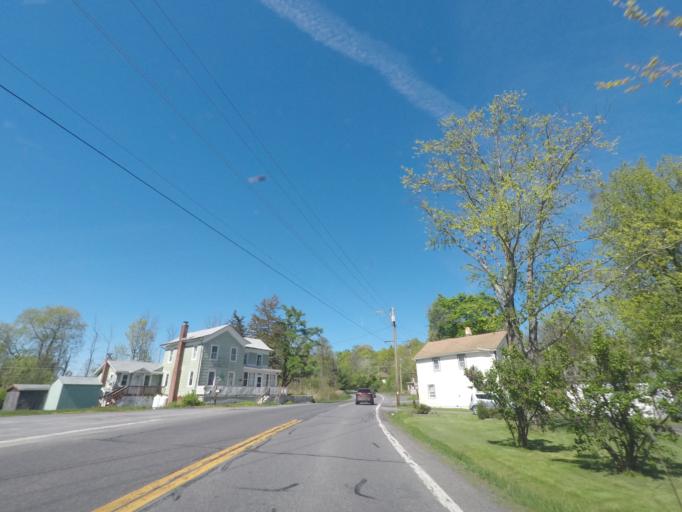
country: US
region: New York
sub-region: Ulster County
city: Saugerties
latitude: 42.1168
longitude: -73.9353
